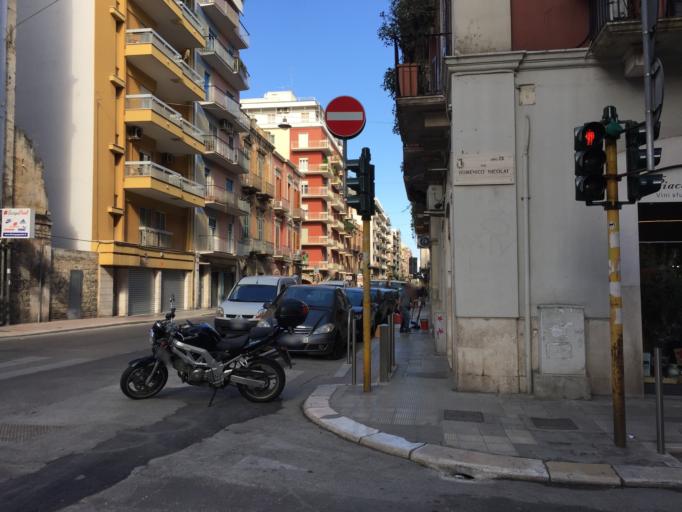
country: IT
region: Apulia
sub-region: Provincia di Bari
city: Bari
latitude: 41.1210
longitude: 16.8645
